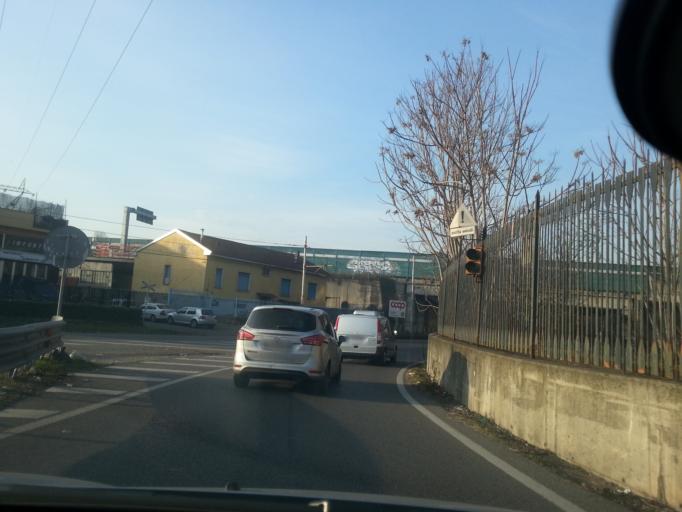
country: IT
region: Lombardy
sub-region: Citta metropolitana di Milano
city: Cormano
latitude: 45.5346
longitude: 9.1613
